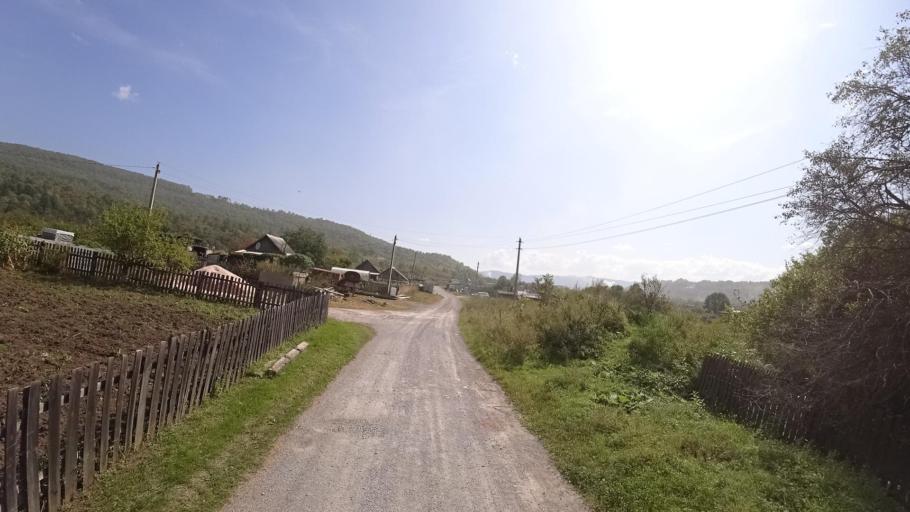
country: RU
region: Jewish Autonomous Oblast
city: Londoko
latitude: 49.0281
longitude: 131.9305
